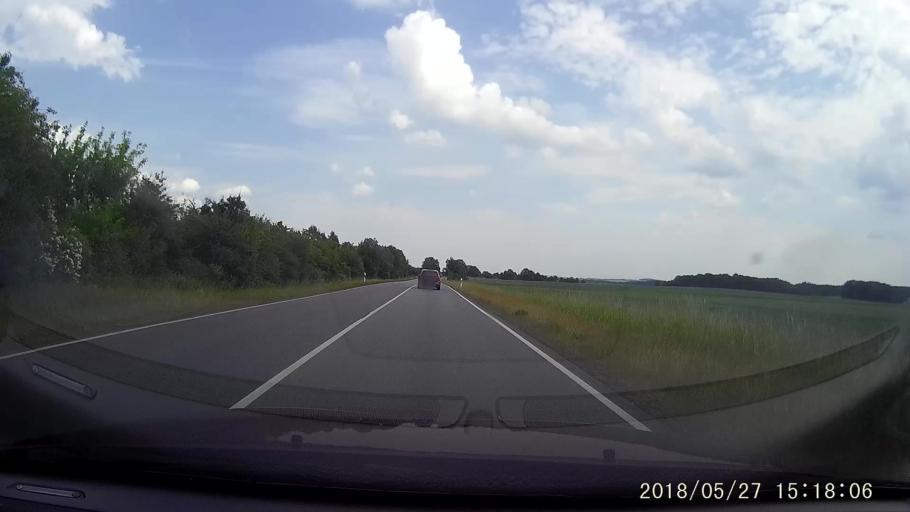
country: DE
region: Saxony
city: Niesky
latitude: 51.2674
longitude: 14.8517
